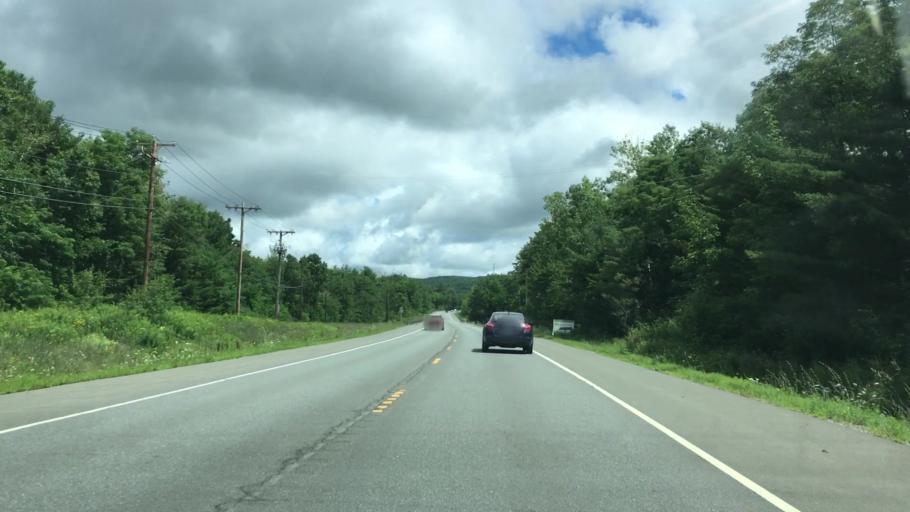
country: US
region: New York
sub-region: Rensselaer County
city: Hoosick Falls
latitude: 42.8490
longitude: -73.4373
